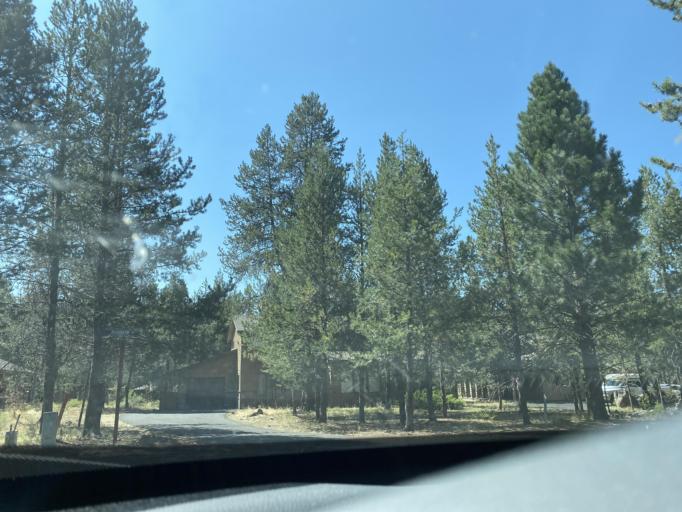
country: US
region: Oregon
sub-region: Deschutes County
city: Sunriver
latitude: 43.8969
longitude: -121.4398
